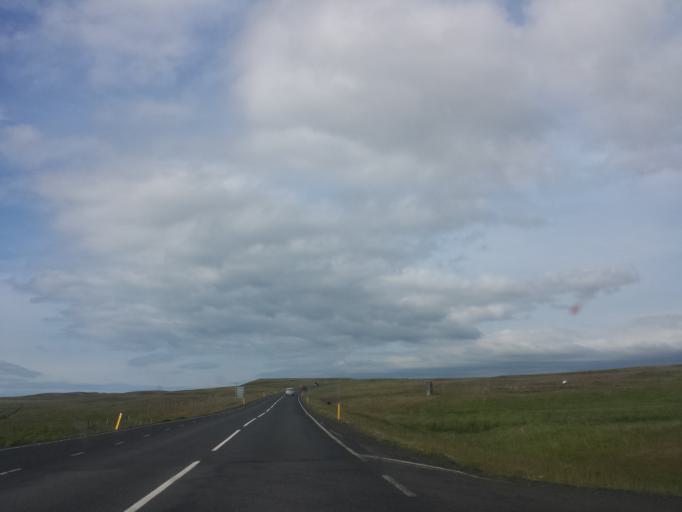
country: IS
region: Northwest
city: Saudarkrokur
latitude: 65.5578
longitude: -20.3409
